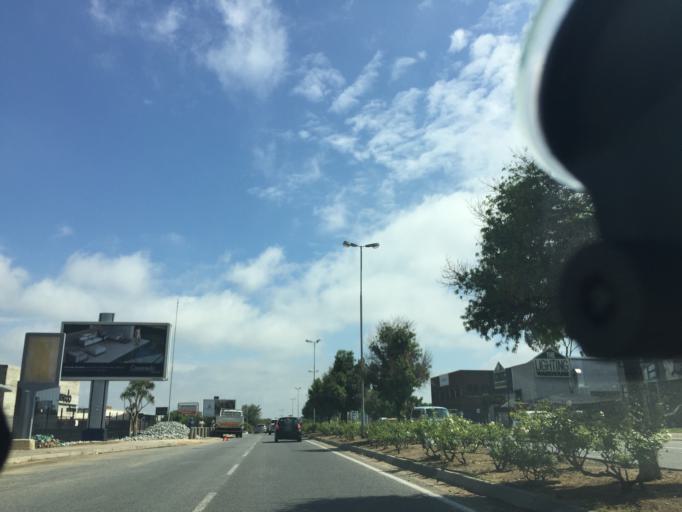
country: ZA
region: Gauteng
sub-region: City of Johannesburg Metropolitan Municipality
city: Modderfontein
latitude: -26.0896
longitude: 28.0794
